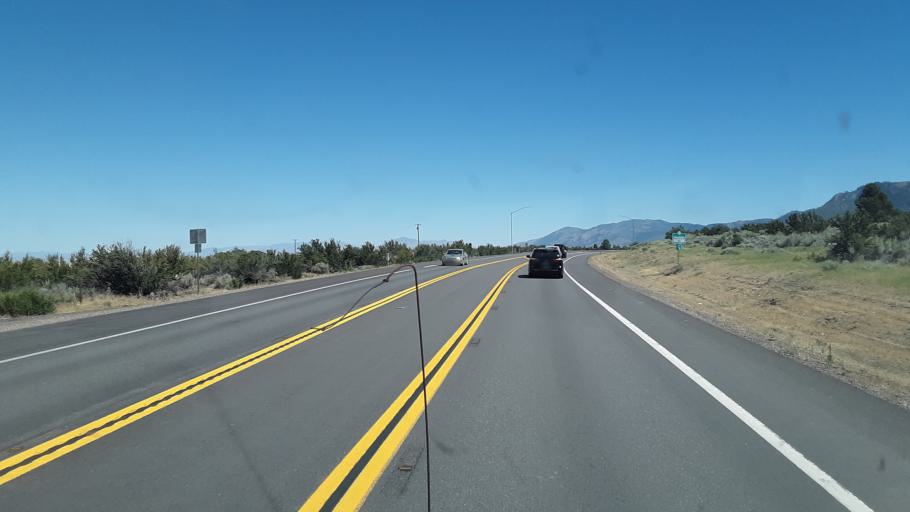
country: US
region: California
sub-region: Lassen County
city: Janesville
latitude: 40.2851
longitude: -120.4920
